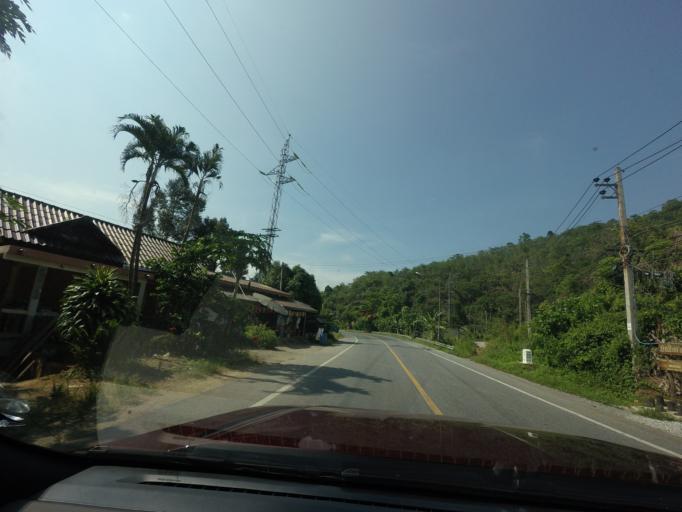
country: TH
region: Yala
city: Than To
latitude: 5.9826
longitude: 101.1987
